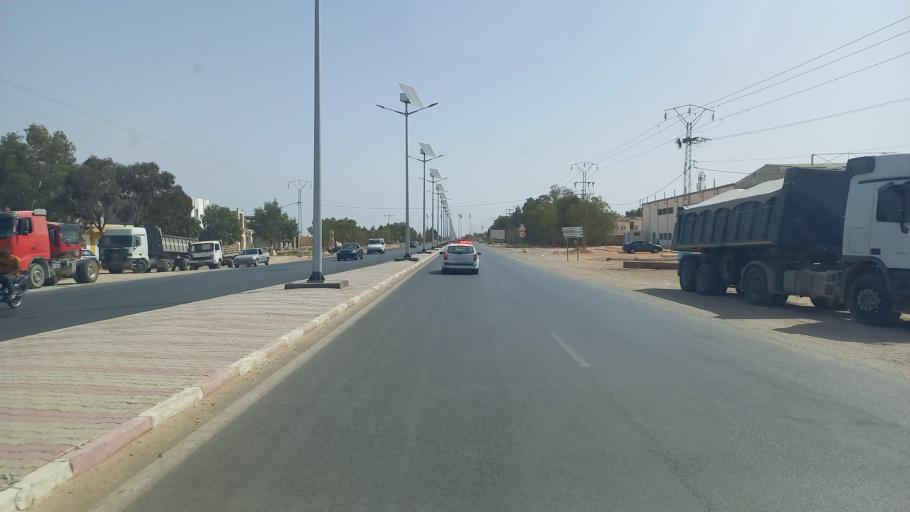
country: TN
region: Madanin
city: Medenine
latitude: 33.3508
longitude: 10.5301
